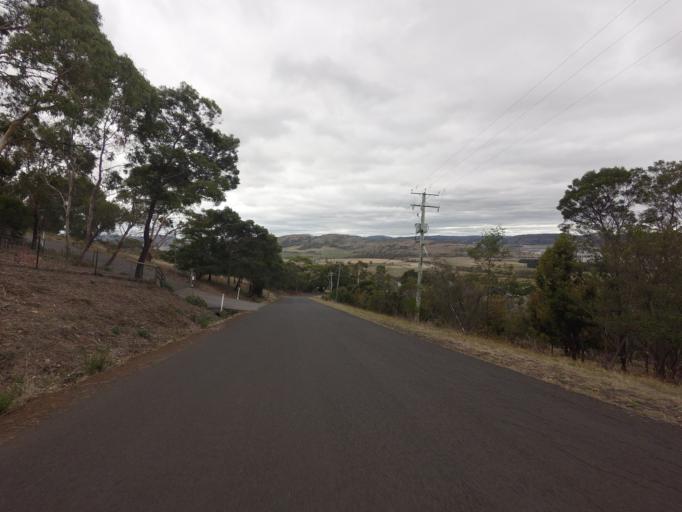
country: AU
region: Tasmania
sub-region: Clarence
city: Cambridge
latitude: -42.7889
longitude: 147.4096
